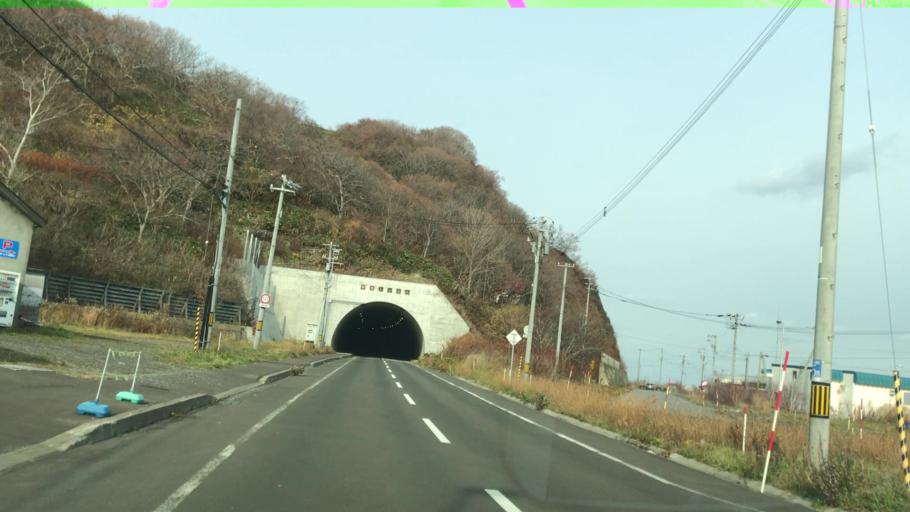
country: JP
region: Hokkaido
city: Iwanai
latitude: 43.3285
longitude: 140.3785
